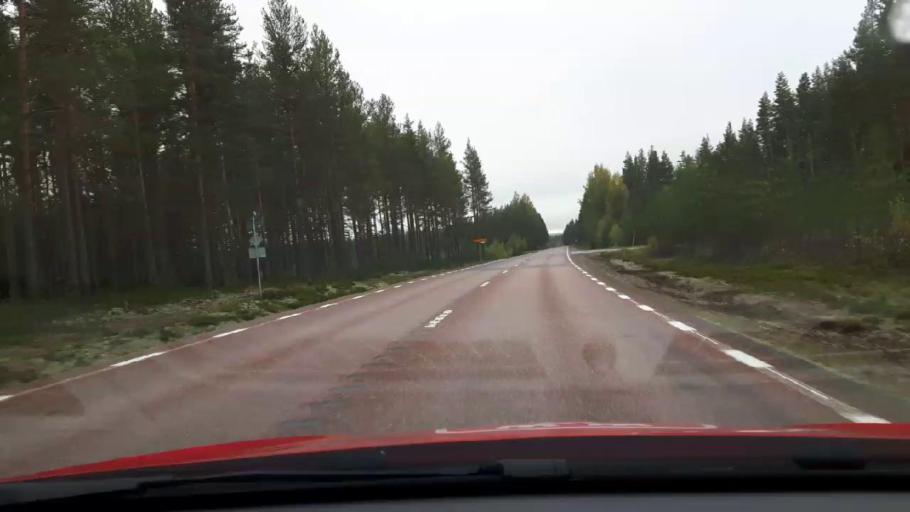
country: SE
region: Gaevleborg
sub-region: Ljusdals Kommun
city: Farila
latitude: 61.8483
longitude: 15.7517
